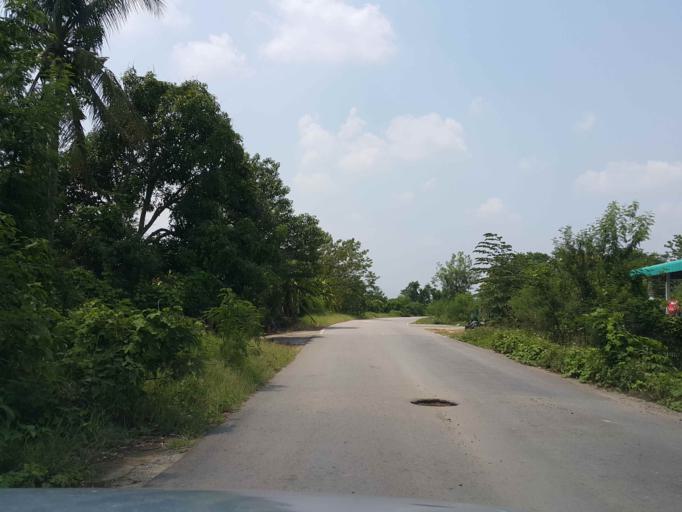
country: TH
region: Chiang Mai
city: Saraphi
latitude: 18.6780
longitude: 99.0058
